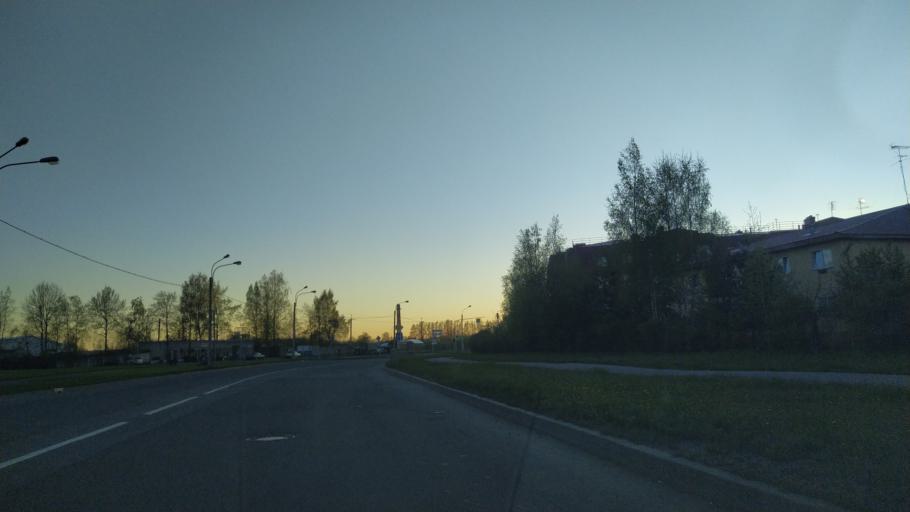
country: RU
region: St.-Petersburg
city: Pushkin
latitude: 59.7005
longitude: 30.3833
